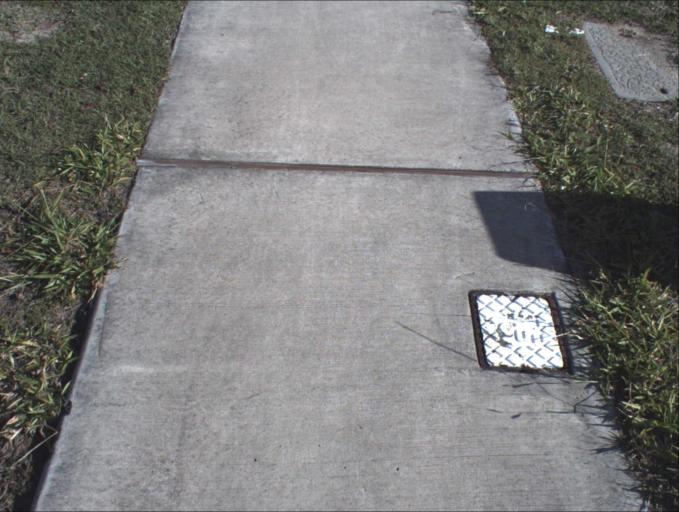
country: AU
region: Queensland
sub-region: Logan
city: Logan Reserve
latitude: -27.6970
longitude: 153.0906
